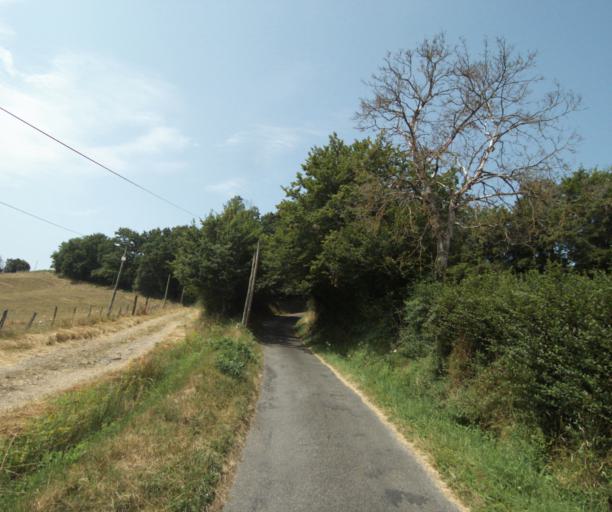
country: FR
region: Bourgogne
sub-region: Departement de Saone-et-Loire
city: Gueugnon
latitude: 46.6151
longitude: 4.0401
